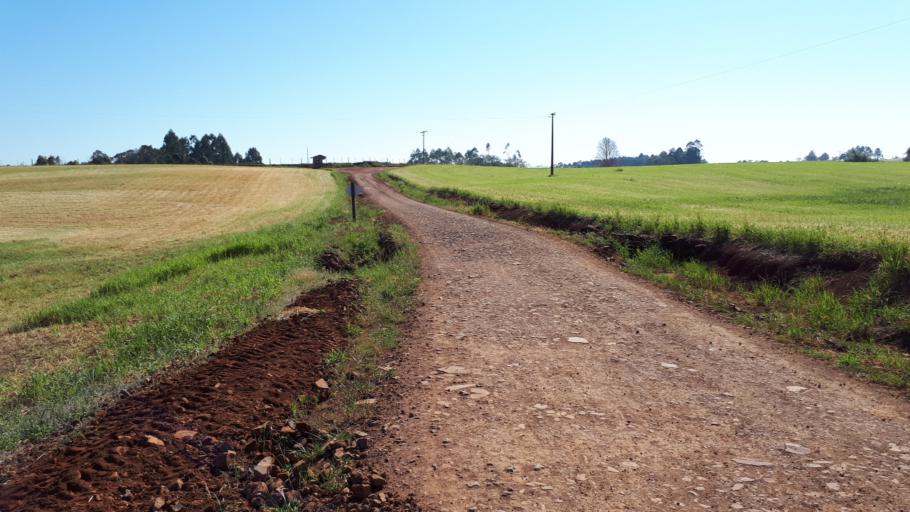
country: AR
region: Misiones
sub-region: Departamento de San Pedro
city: San Pedro
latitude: -26.8431
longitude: -53.6481
